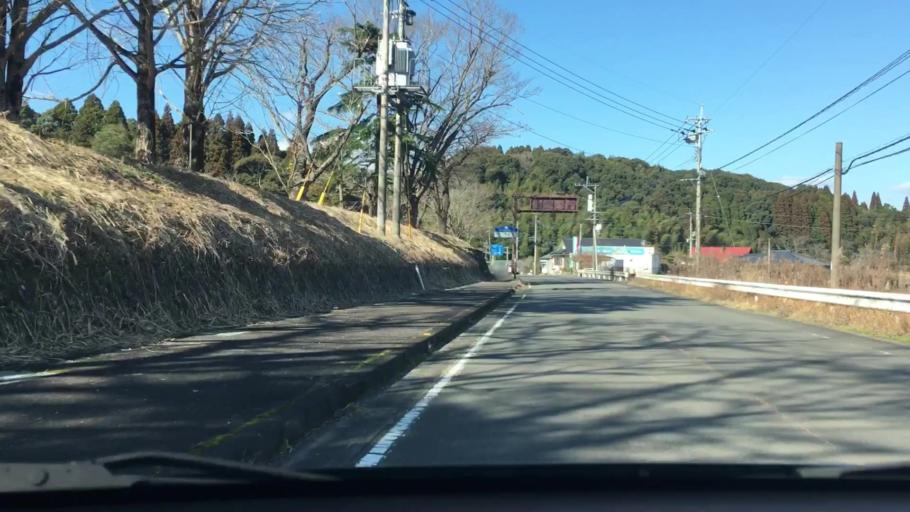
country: JP
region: Kagoshima
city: Satsumasendai
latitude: 31.7769
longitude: 130.4007
